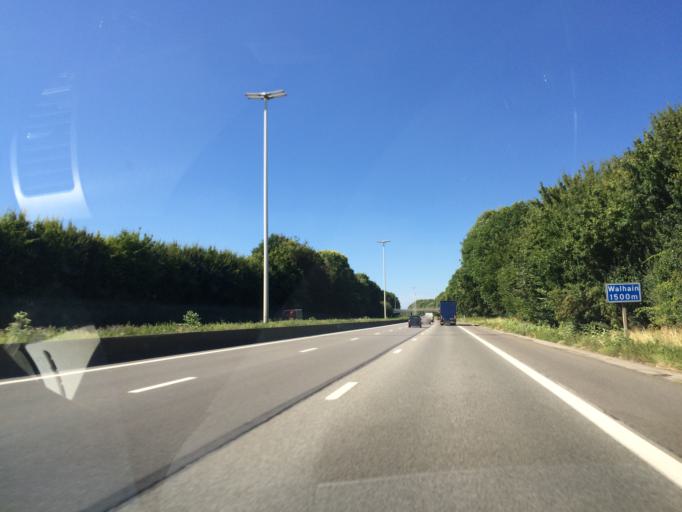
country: BE
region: Wallonia
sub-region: Province du Brabant Wallon
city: Walhain-Saint-Paul
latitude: 50.6323
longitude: 4.7499
